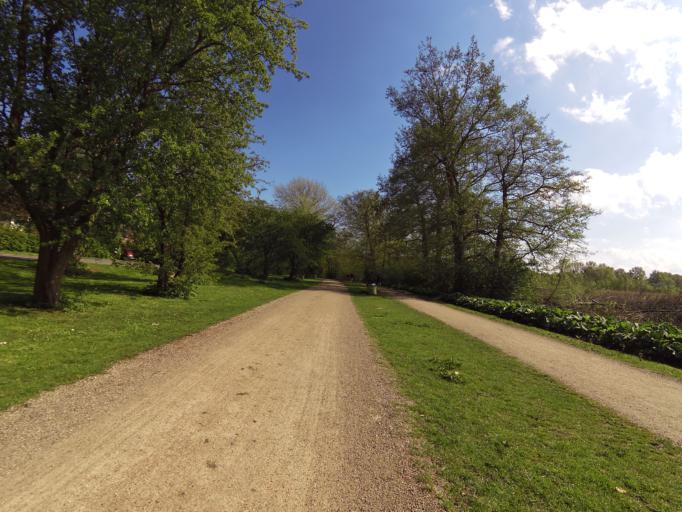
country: DK
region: Capital Region
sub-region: Frederiksberg Kommune
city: Frederiksberg
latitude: 55.7213
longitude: 12.5237
